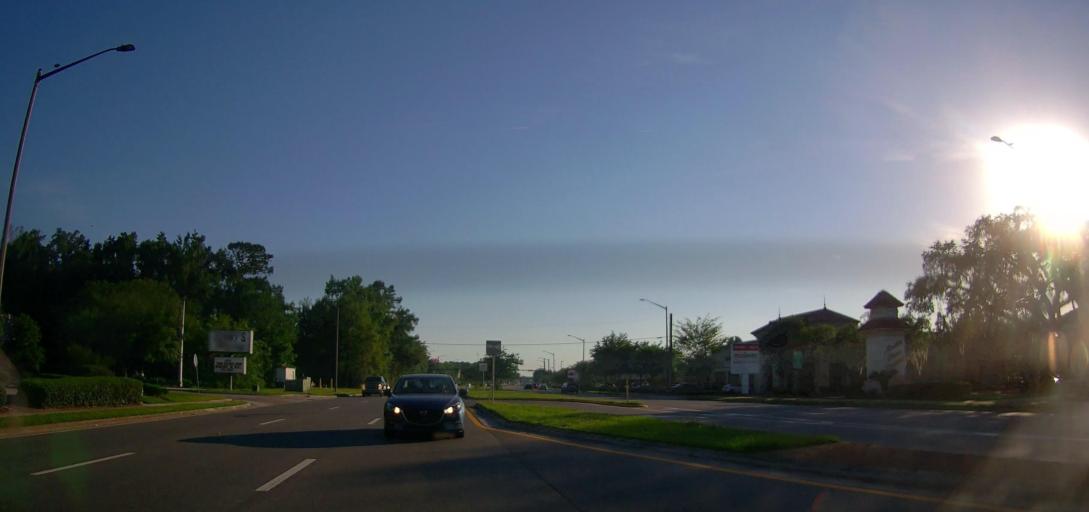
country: US
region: Florida
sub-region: Alachua County
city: Gainesville
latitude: 29.6216
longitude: -82.3776
